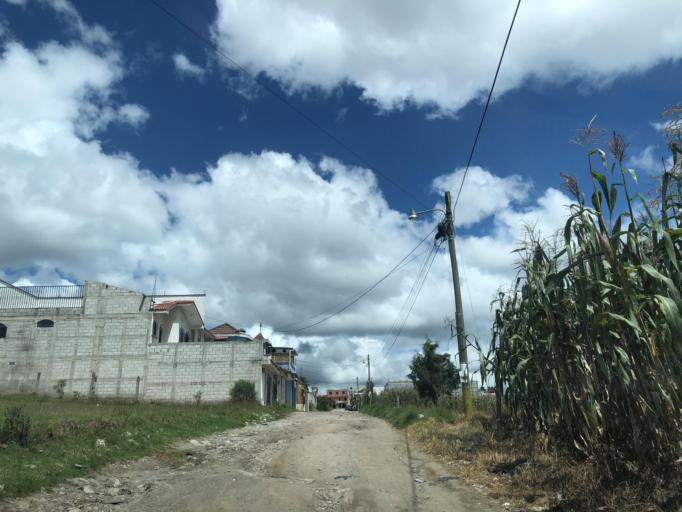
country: GT
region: Quetzaltenango
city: Quetzaltenango
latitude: 14.8391
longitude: -91.5444
